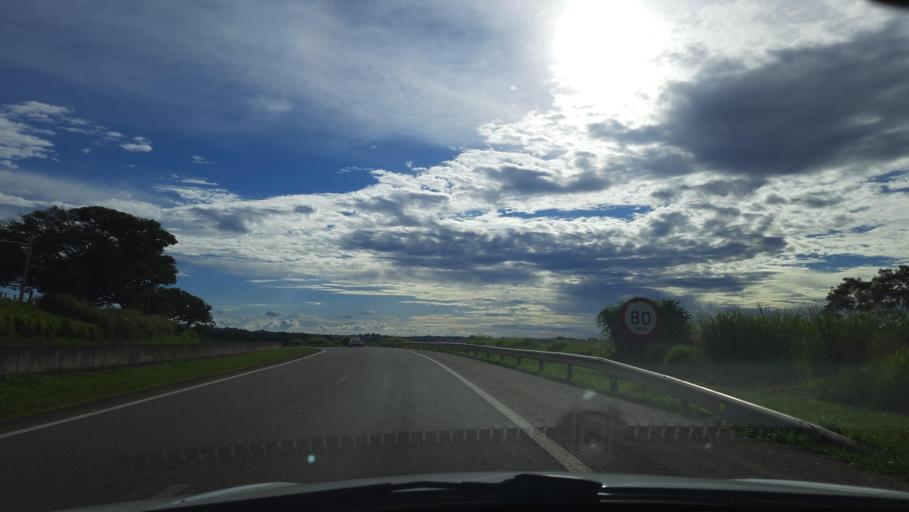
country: BR
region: Sao Paulo
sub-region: Sao Joao Da Boa Vista
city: Sao Joao da Boa Vista
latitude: -21.9526
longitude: -46.7287
